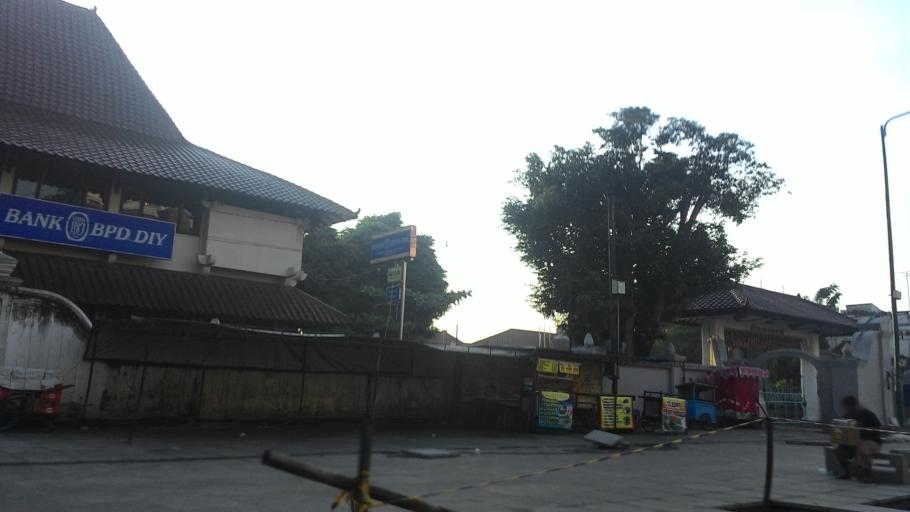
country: ID
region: Daerah Istimewa Yogyakarta
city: Yogyakarta
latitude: -7.7955
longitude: 110.3655
